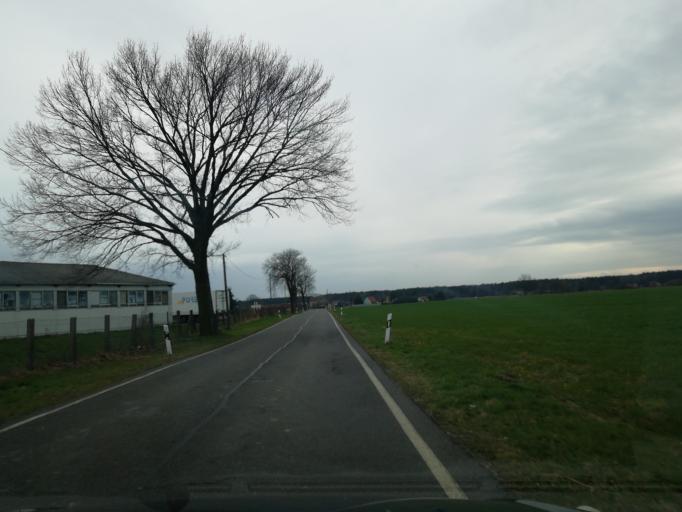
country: DE
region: Brandenburg
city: Calau
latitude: 51.7358
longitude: 14.0200
